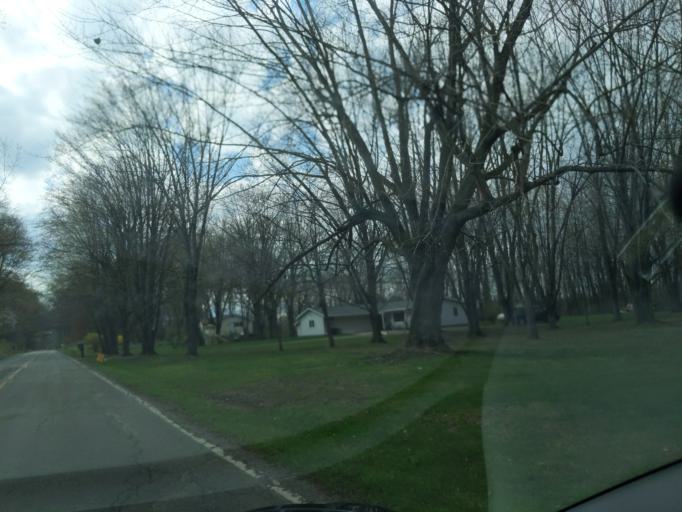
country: US
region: Michigan
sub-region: Jackson County
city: Jackson
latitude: 42.3420
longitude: -84.3852
